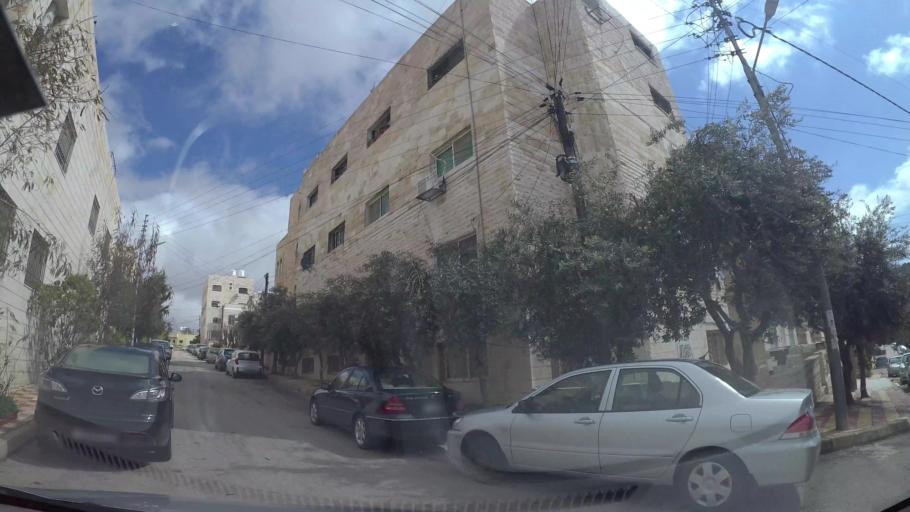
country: JO
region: Amman
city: Al Jubayhah
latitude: 32.0627
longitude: 35.8761
